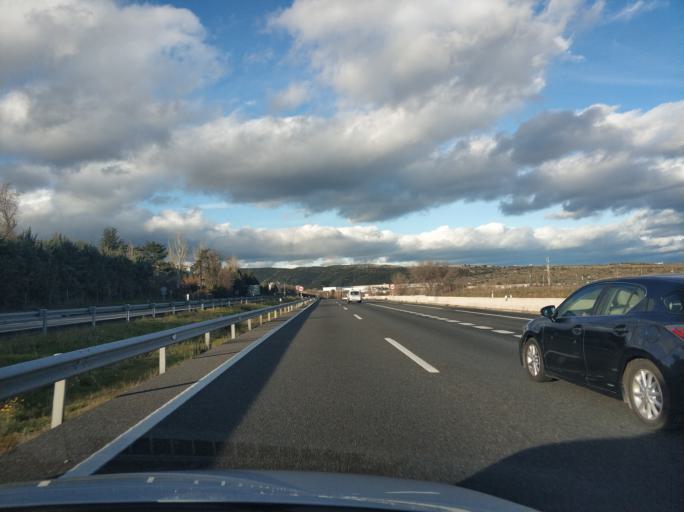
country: ES
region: Madrid
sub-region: Provincia de Madrid
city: San Agustin de Guadalix
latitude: 40.6790
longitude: -3.6109
